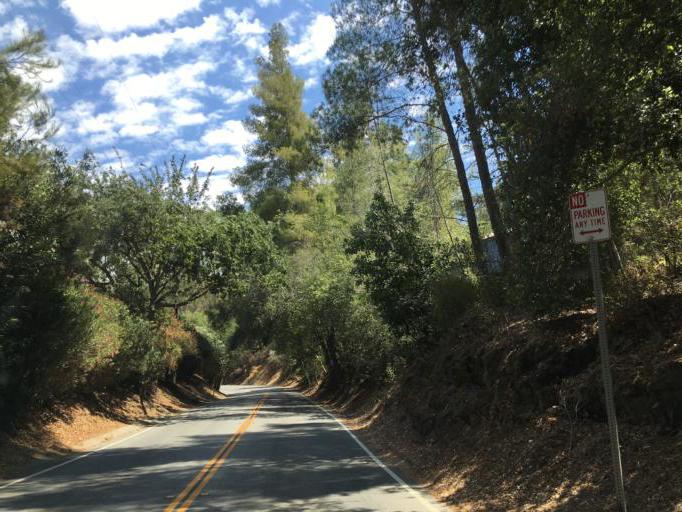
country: US
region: California
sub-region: Los Angeles County
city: Agoura Hills
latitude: 34.1095
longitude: -118.7538
